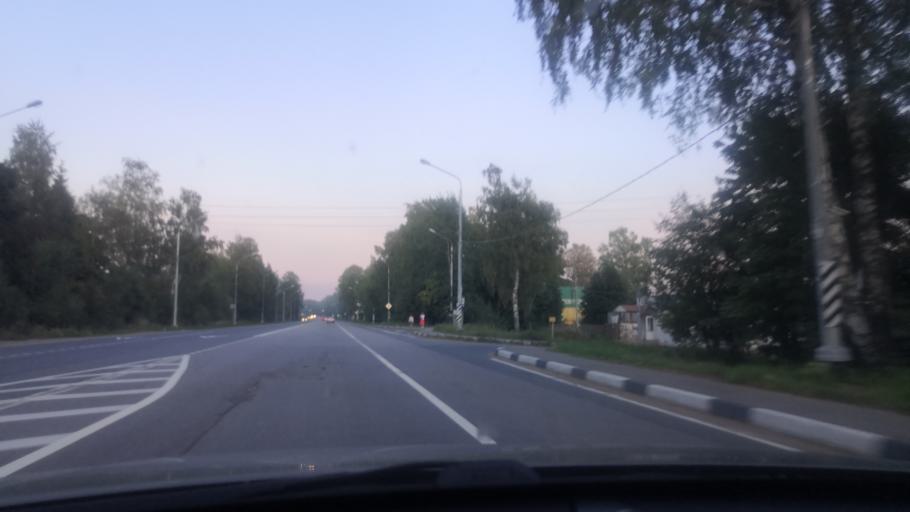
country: RU
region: St.-Petersburg
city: Beloostrov
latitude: 60.1962
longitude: 30.0484
